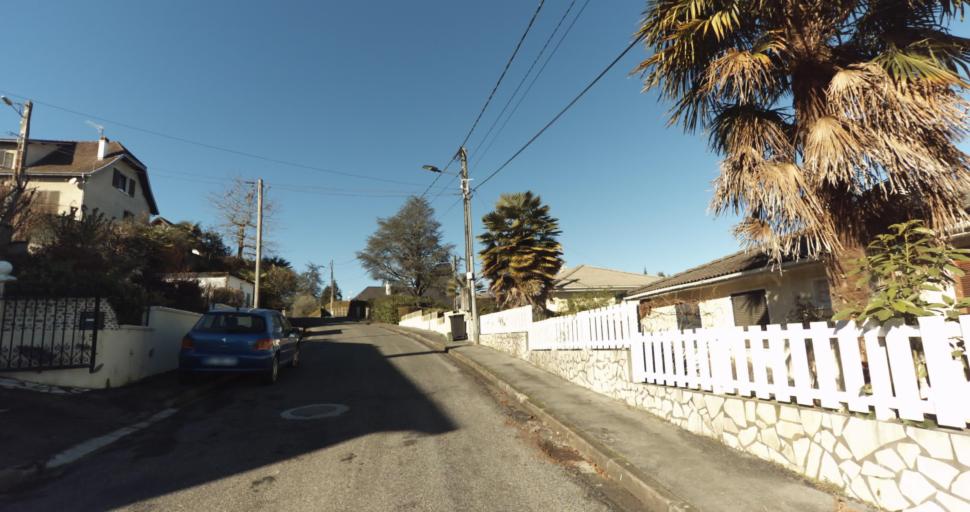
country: FR
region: Aquitaine
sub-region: Departement des Pyrenees-Atlantiques
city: Morlaas
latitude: 43.3427
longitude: -0.2696
